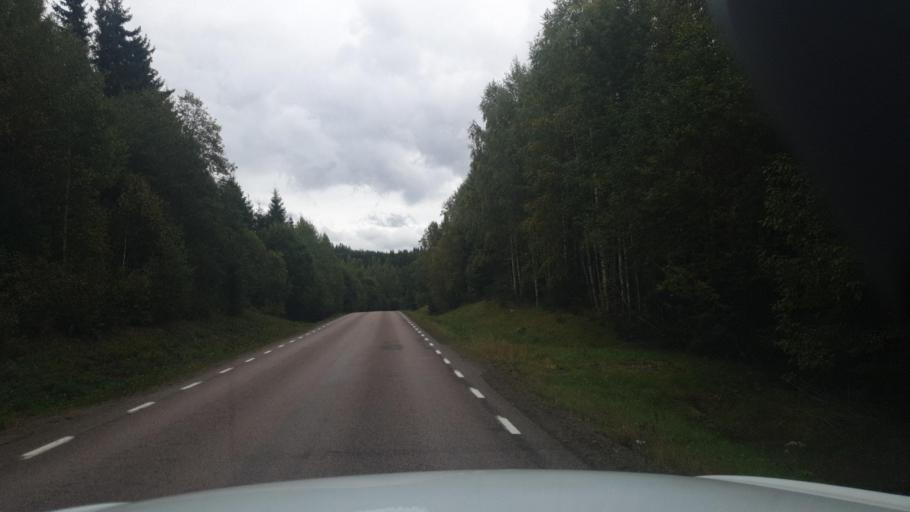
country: SE
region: Vaermland
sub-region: Arvika Kommun
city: Arvika
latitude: 59.9524
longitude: 12.7314
